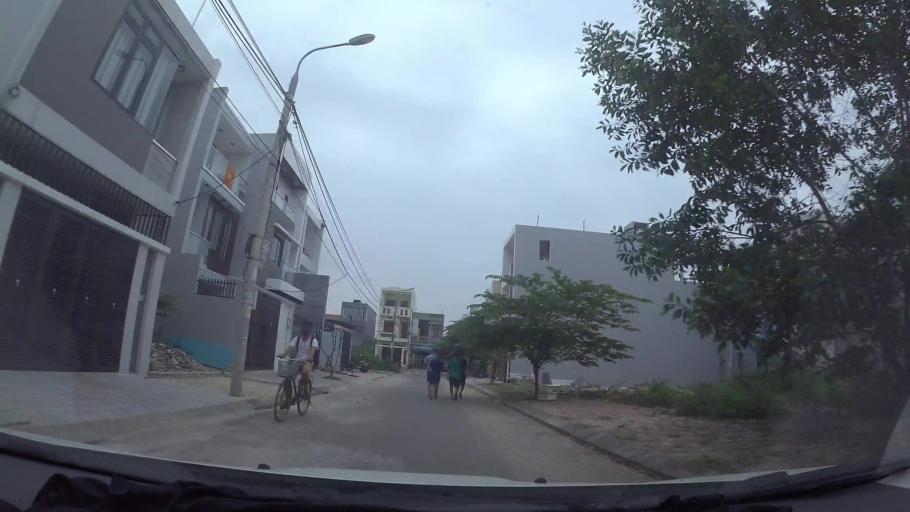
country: VN
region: Da Nang
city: Lien Chieu
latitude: 16.0778
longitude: 108.1564
